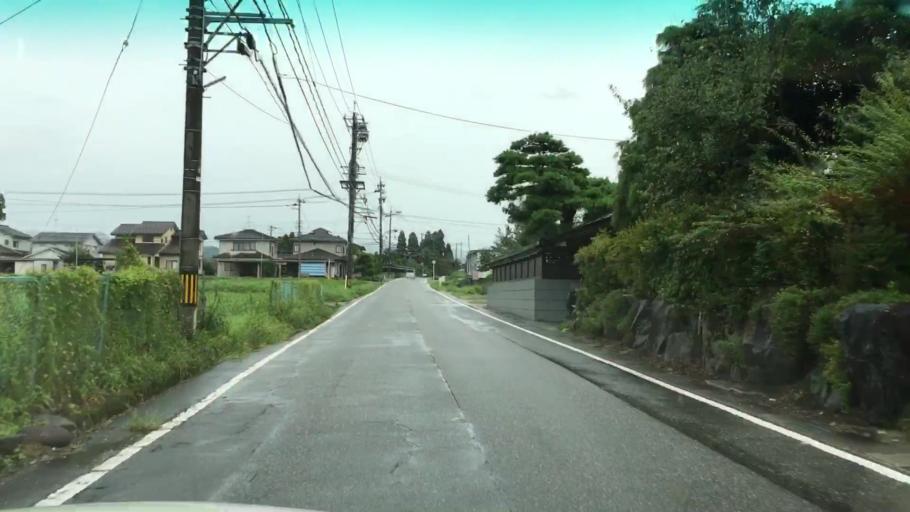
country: JP
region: Toyama
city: Kamiichi
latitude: 36.6429
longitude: 137.3204
